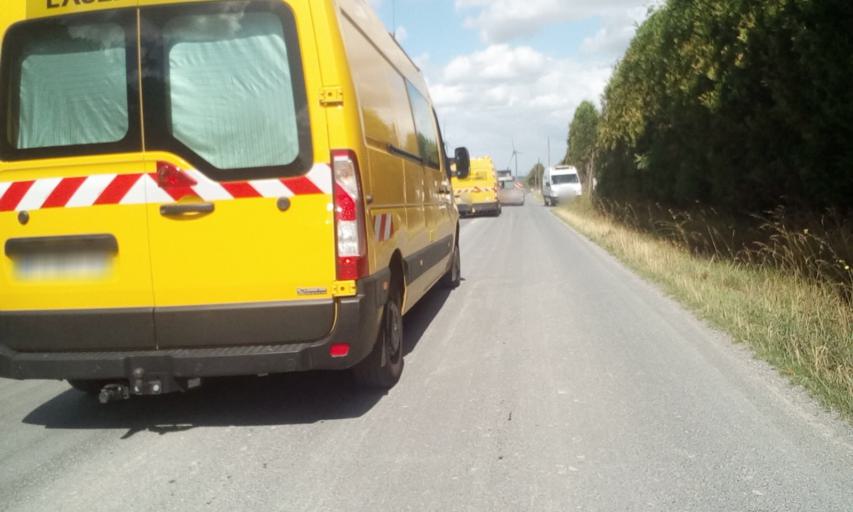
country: FR
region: Lower Normandy
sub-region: Departement du Calvados
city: Cagny
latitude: 49.1110
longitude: -0.2636
